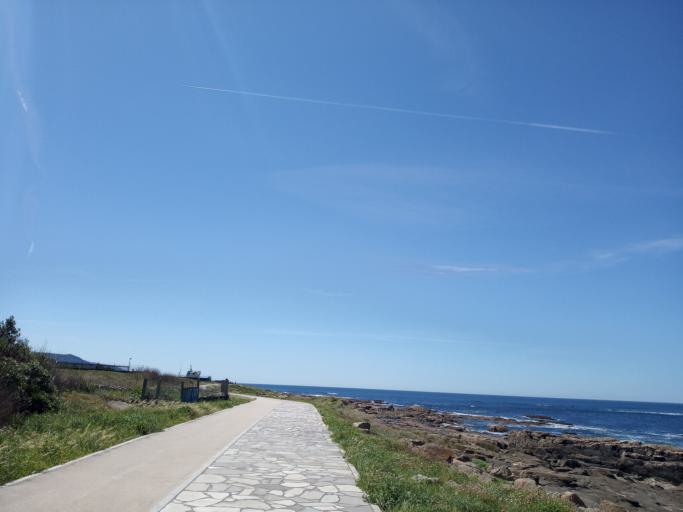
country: ES
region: Galicia
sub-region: Provincia de Pontevedra
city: A Guarda
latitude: 41.8860
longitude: -8.8812
